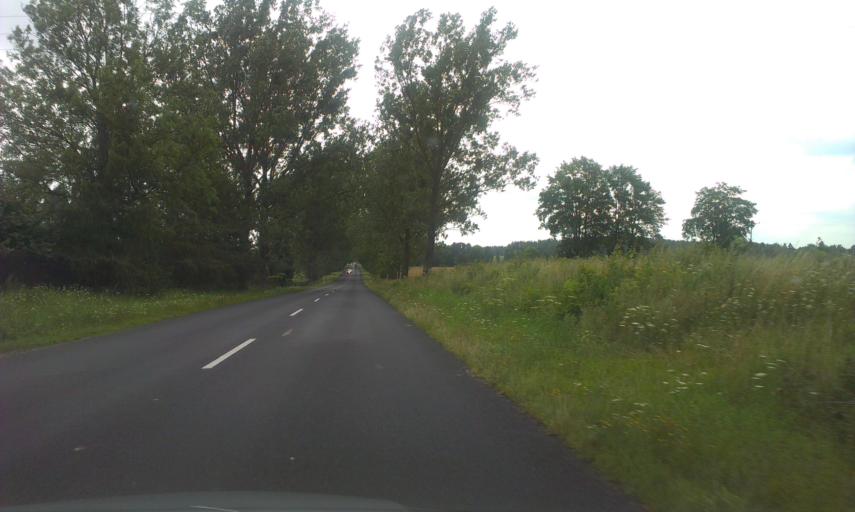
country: PL
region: West Pomeranian Voivodeship
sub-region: Powiat swidwinski
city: Polczyn-Zdroj
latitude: 53.8362
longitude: 16.0768
